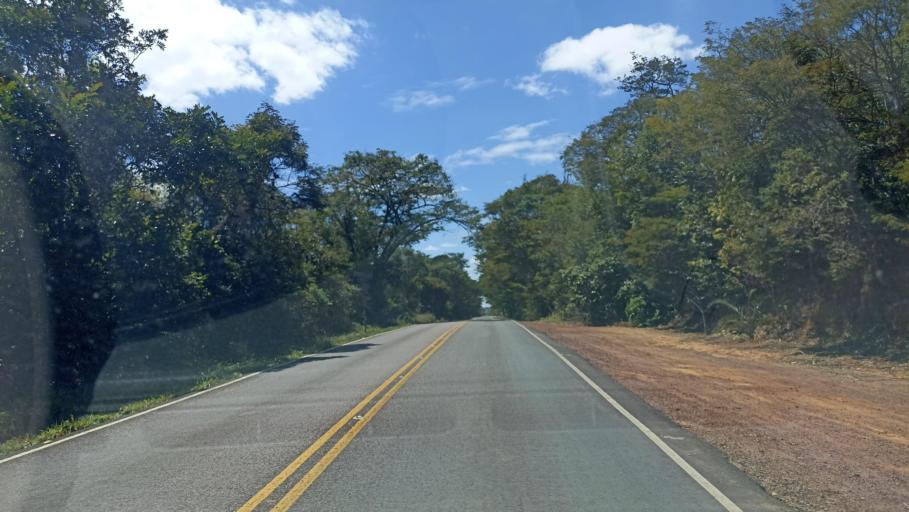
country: BR
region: Bahia
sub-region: Andarai
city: Vera Cruz
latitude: -12.7685
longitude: -41.3301
